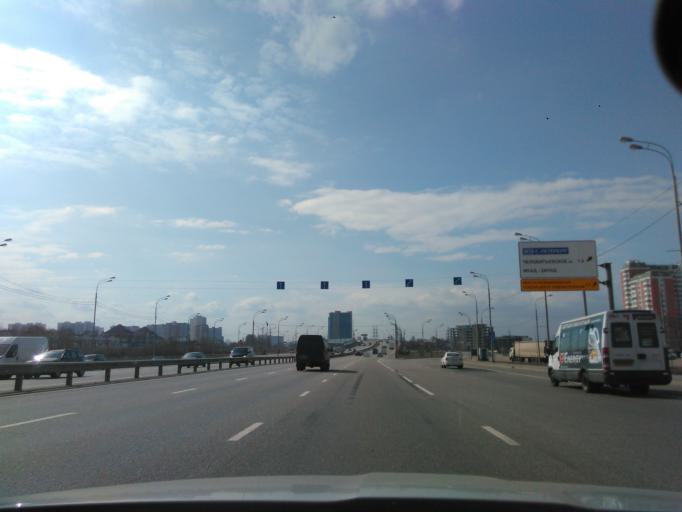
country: RU
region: Moscow
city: Severnyy
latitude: 55.9244
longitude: 37.5459
